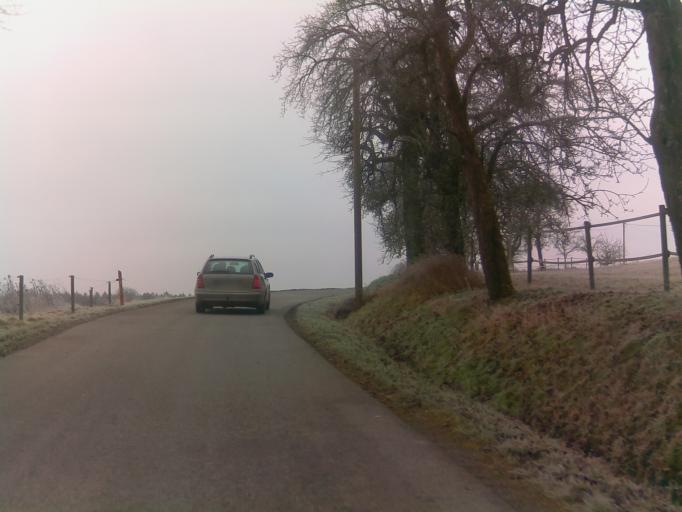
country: DE
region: Baden-Wuerttemberg
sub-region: Karlsruhe Region
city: Seckach
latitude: 49.4705
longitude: 9.3104
